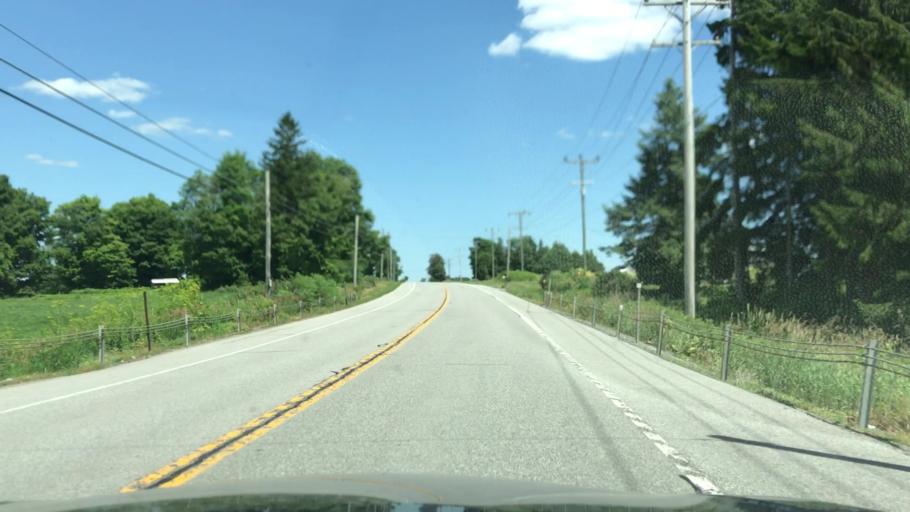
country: US
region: New York
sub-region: Wyoming County
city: Perry
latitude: 42.7440
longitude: -78.0616
